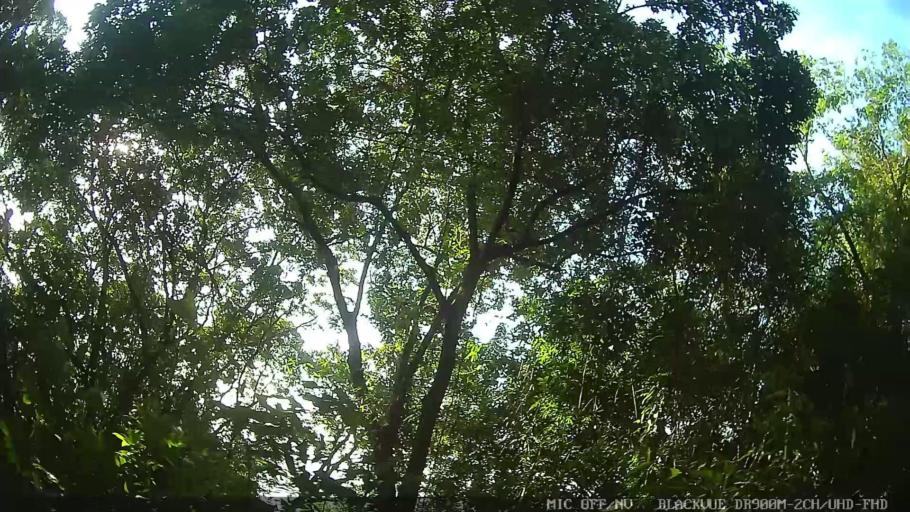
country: BR
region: Sao Paulo
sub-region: Guaruja
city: Guaruja
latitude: -23.9821
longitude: -46.2561
